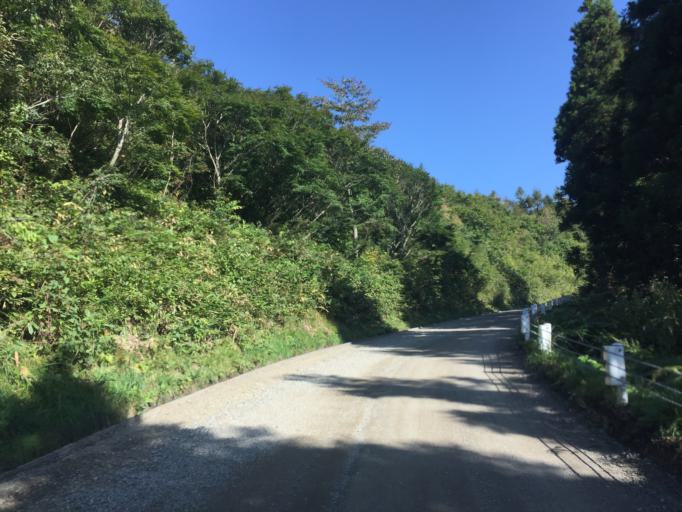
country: JP
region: Fukushima
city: Inawashiro
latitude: 37.4597
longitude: 139.9936
